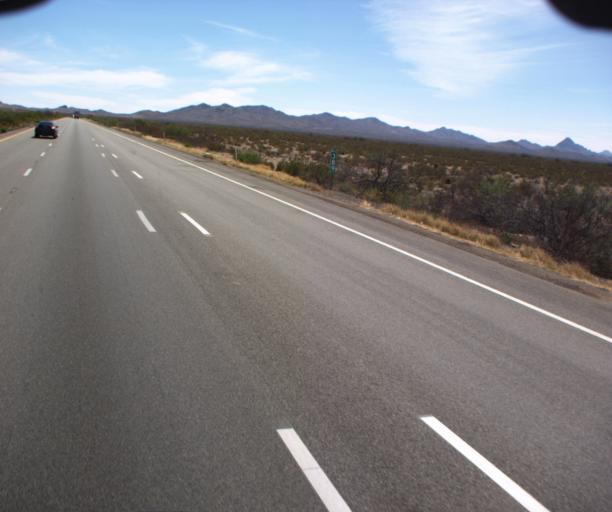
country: US
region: New Mexico
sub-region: Hidalgo County
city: Lordsburg
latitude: 32.2358
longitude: -109.0852
